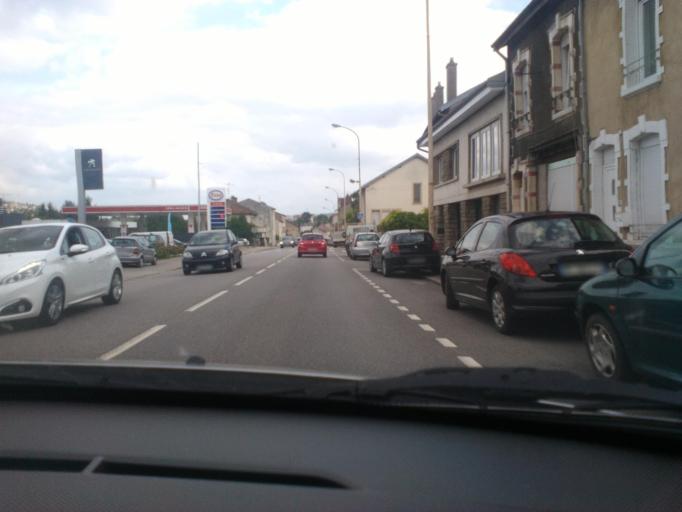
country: FR
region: Lorraine
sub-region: Departement de Meurthe-et-Moselle
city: Frouard
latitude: 48.7585
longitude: 6.1352
